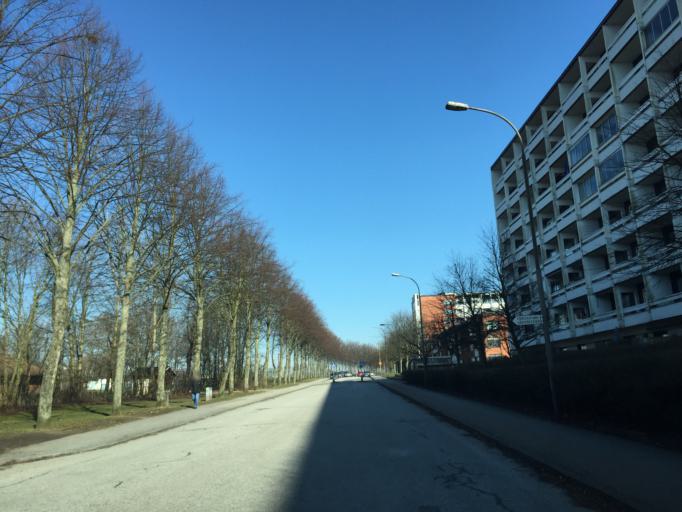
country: SE
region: Skane
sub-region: Lunds Kommun
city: Lund
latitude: 55.6918
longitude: 13.1714
